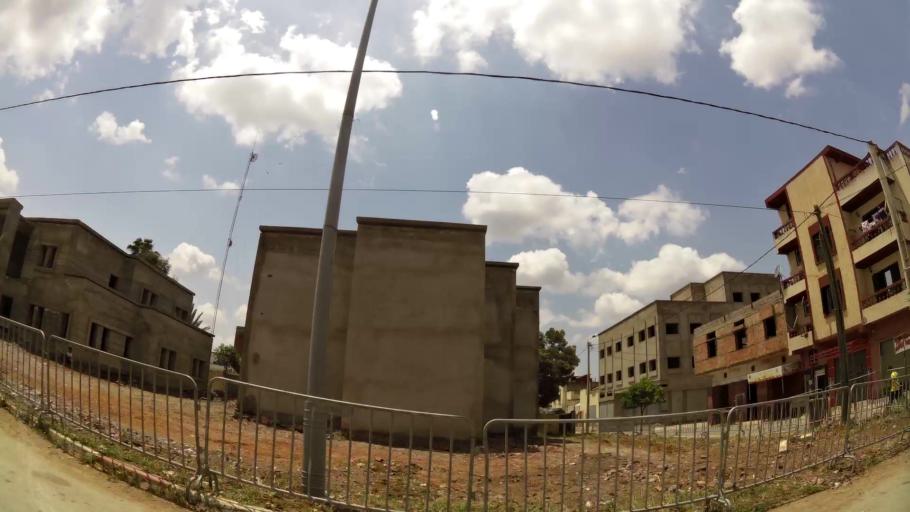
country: MA
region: Rabat-Sale-Zemmour-Zaer
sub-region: Khemisset
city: Tiflet
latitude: 34.0040
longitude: -6.5273
